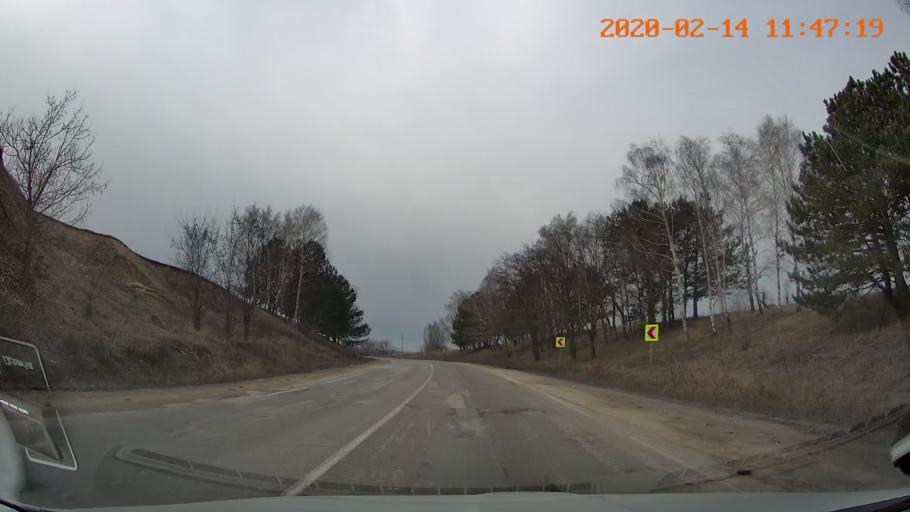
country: MD
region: Briceni
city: Briceni
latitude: 48.3167
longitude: 26.9722
